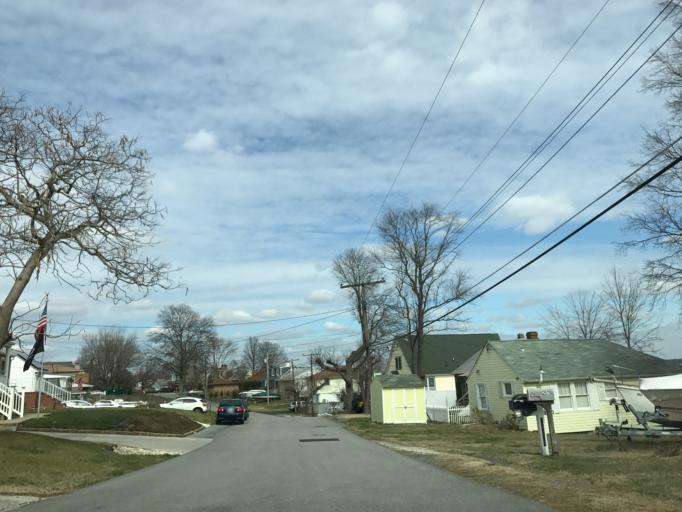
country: US
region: Maryland
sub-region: Baltimore County
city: Bowleys Quarters
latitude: 39.3009
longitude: -76.4094
